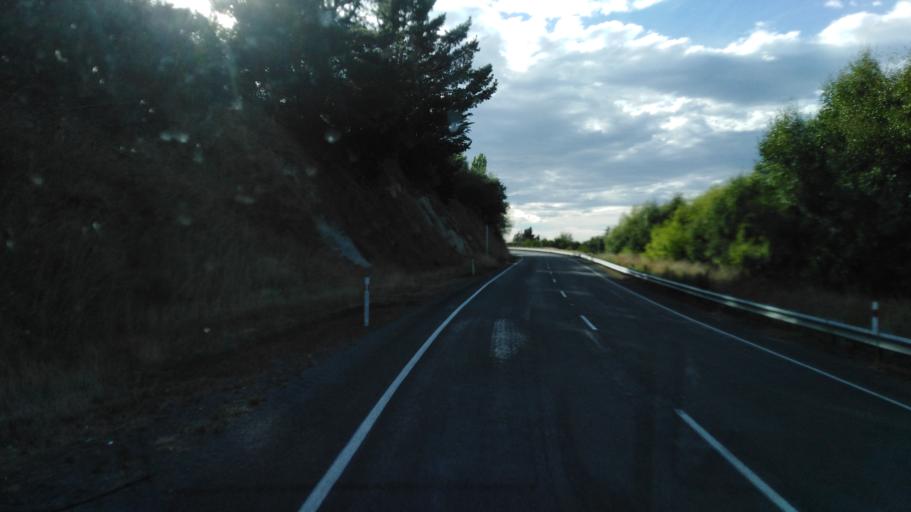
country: NZ
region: Canterbury
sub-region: Hurunui District
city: Amberley
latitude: -42.8705
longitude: 173.2031
